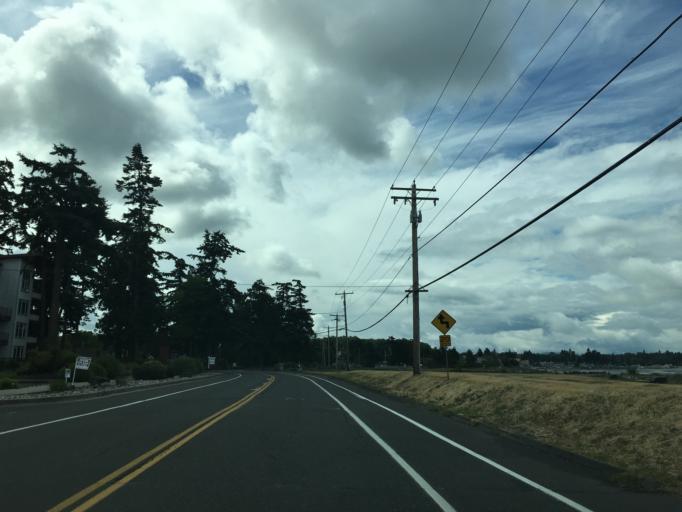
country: US
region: Washington
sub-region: Whatcom County
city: Birch Bay
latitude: 48.9223
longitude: -122.7450
